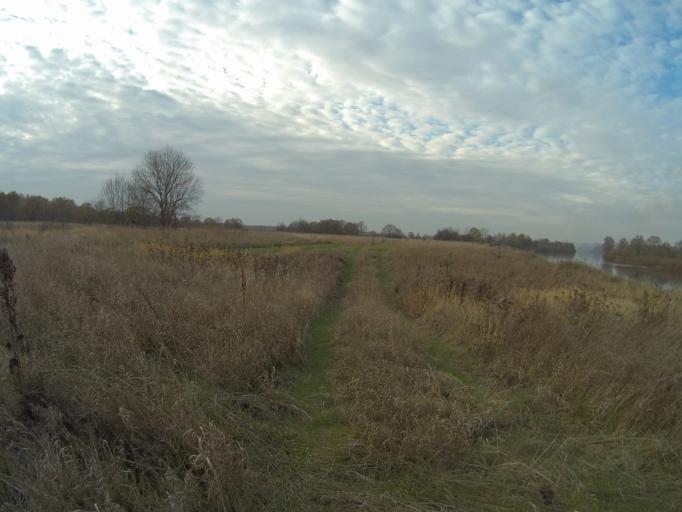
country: RU
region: Vladimir
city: Orgtrud
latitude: 56.1694
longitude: 40.6133
